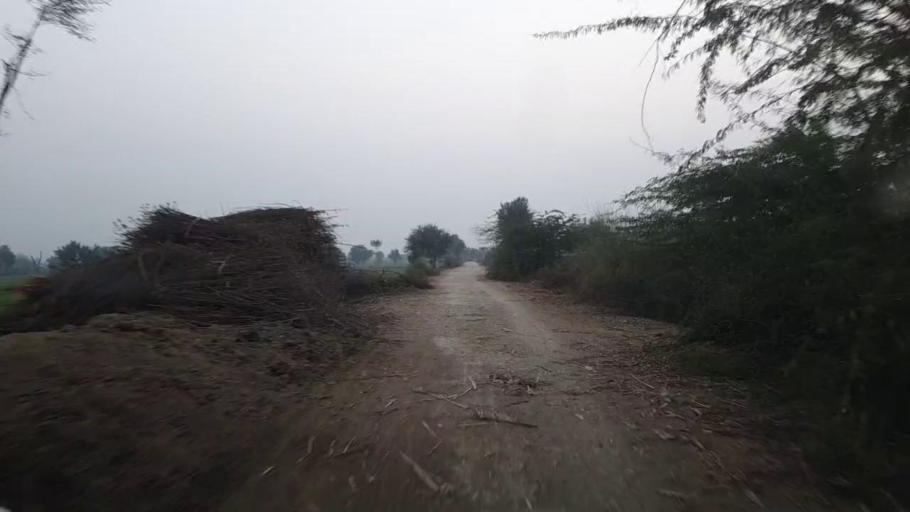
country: PK
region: Sindh
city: Karaundi
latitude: 26.9484
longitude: 68.4487
